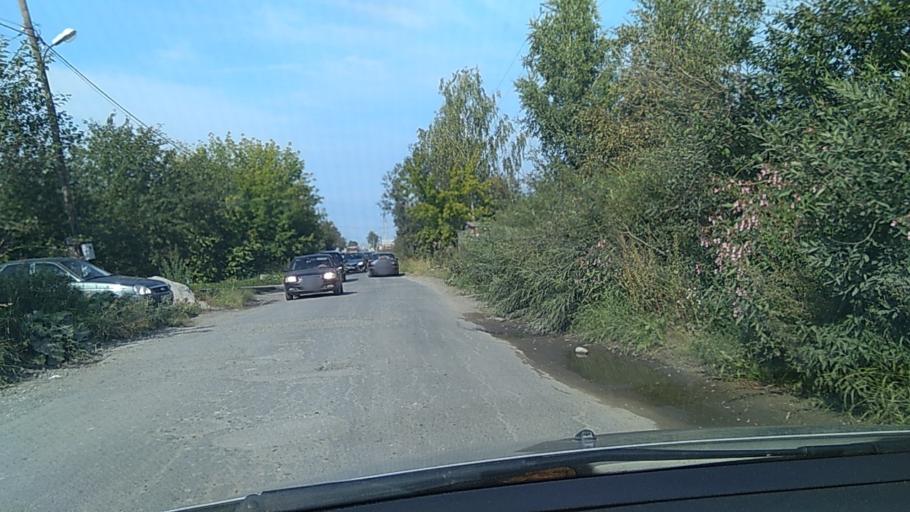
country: RU
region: Sverdlovsk
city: Sredneuralsk
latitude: 56.9771
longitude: 60.4749
